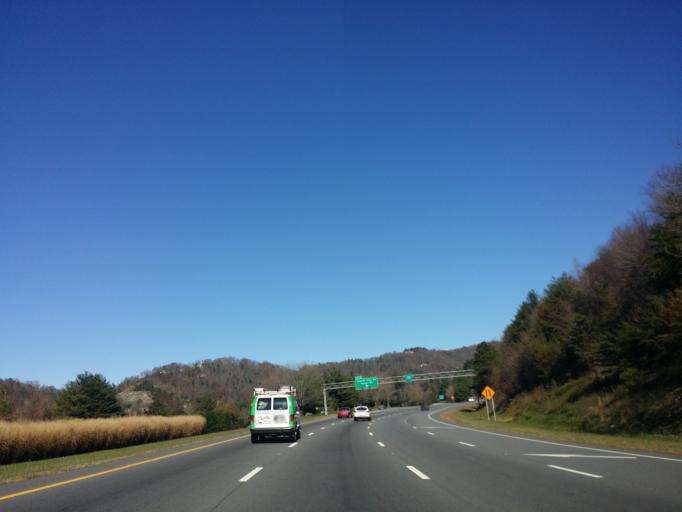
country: US
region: North Carolina
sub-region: Buncombe County
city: Asheville
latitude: 35.5901
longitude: -82.5269
